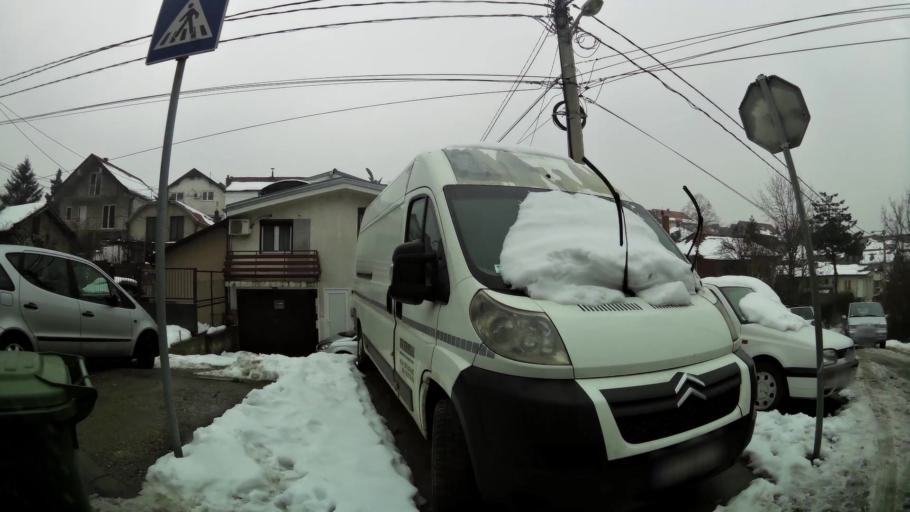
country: RS
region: Central Serbia
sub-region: Belgrade
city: Zvezdara
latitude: 44.7821
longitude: 20.5162
